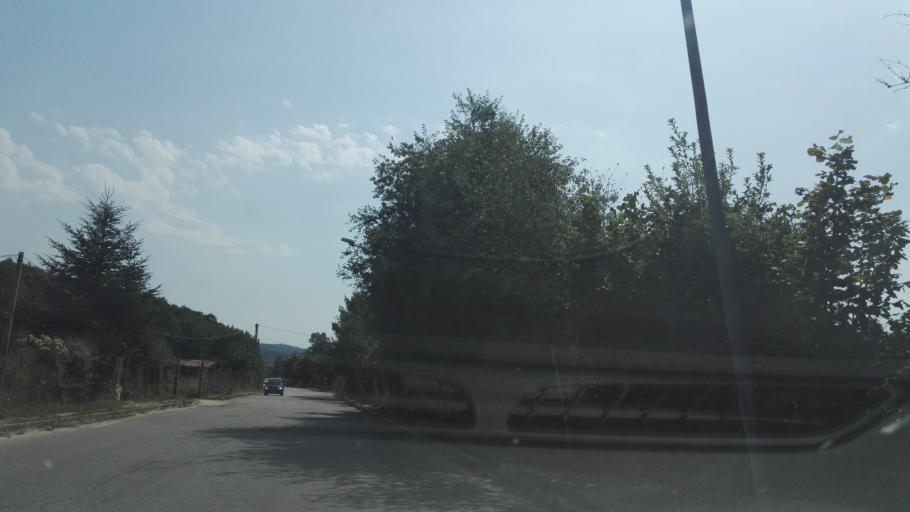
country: IT
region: Calabria
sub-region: Provincia di Vibo-Valentia
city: Serra San Bruno
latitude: 38.5746
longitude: 16.3315
